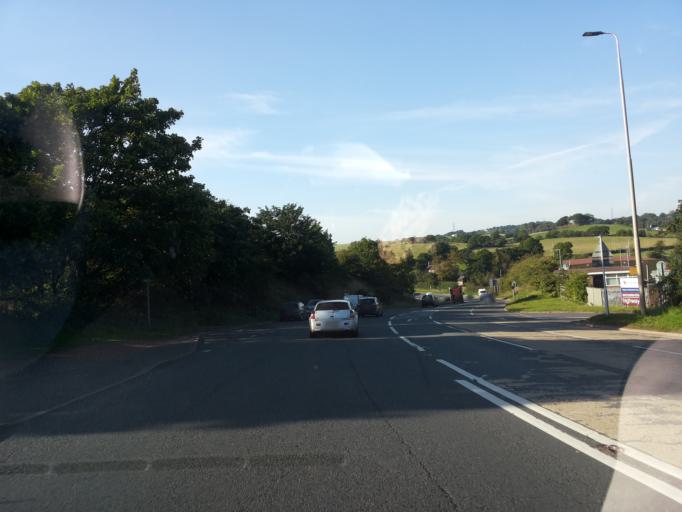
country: GB
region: England
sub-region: Worcestershire
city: Bromsgrove
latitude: 52.3790
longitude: -2.0476
